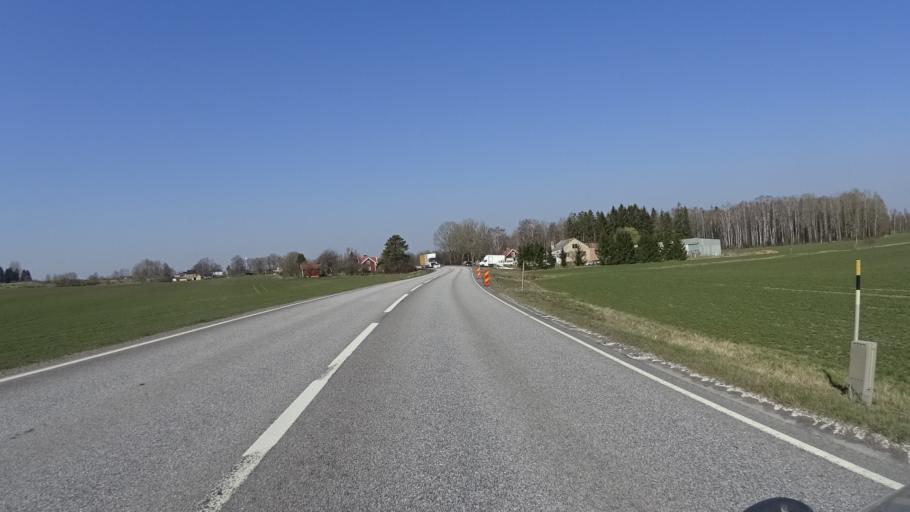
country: SE
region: OEstergoetland
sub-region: Mjolby Kommun
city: Mantorp
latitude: 58.3773
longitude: 15.2616
